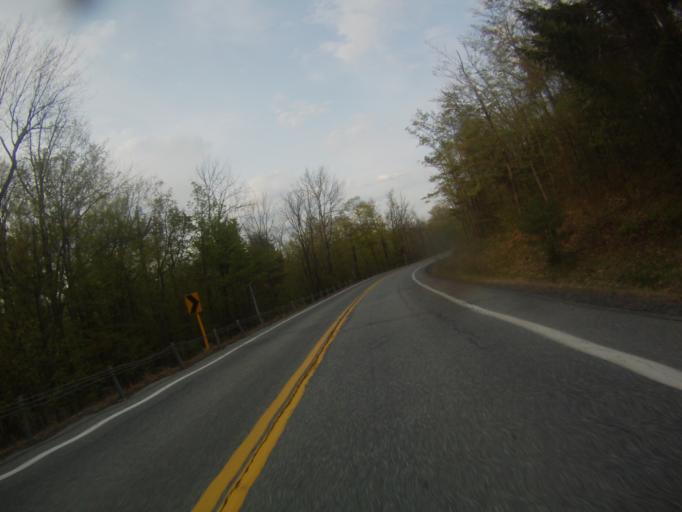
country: US
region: New York
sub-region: Essex County
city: Ticonderoga
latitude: 43.7503
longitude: -73.5709
